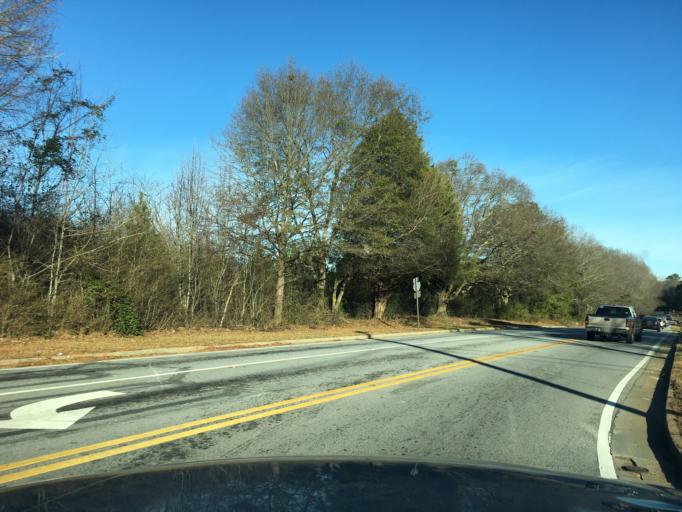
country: US
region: Georgia
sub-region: Rockdale County
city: Conyers
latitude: 33.6611
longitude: -84.0497
